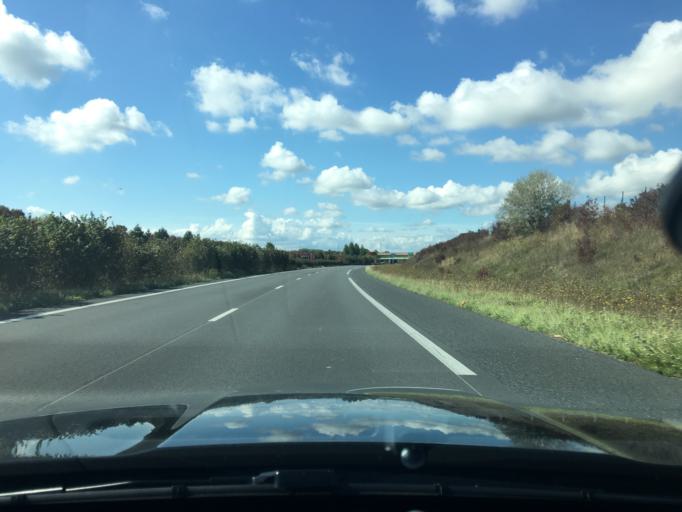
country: FR
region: Ile-de-France
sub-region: Departement du Val-d'Oise
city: Louvres
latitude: 49.0272
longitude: 2.5114
